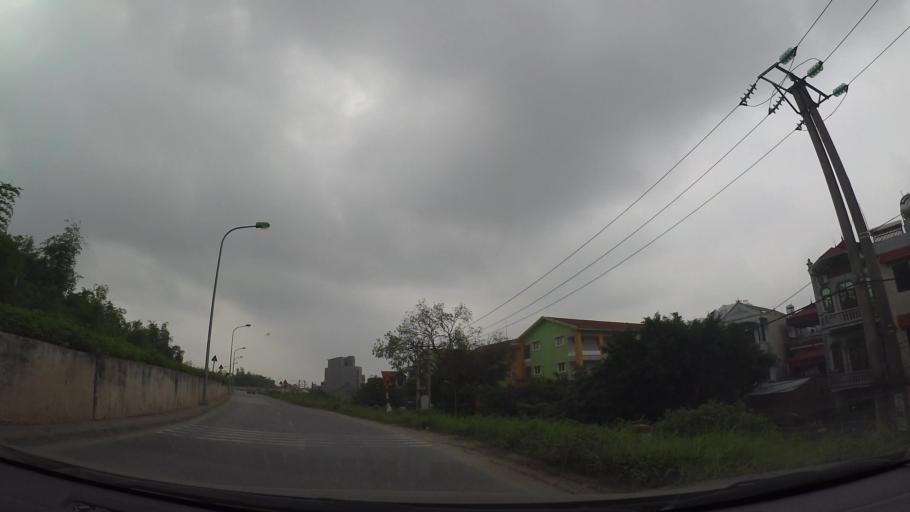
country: VN
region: Ha Noi
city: Trau Quy
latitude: 21.0407
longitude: 105.9325
